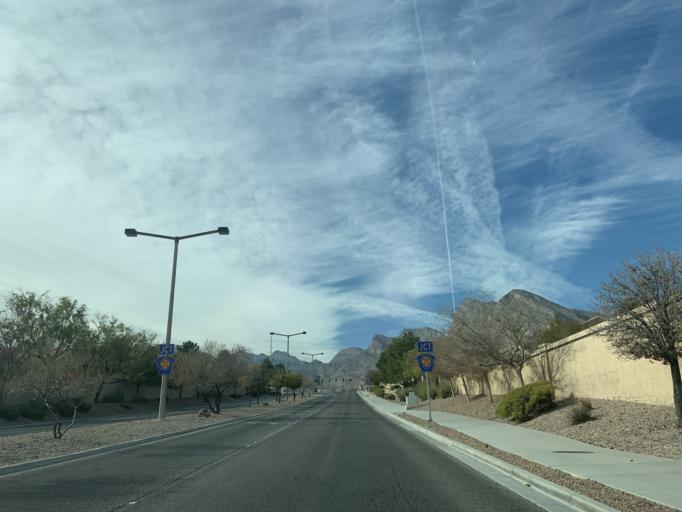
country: US
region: Nevada
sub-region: Clark County
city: Summerlin South
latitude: 36.2049
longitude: -115.3373
